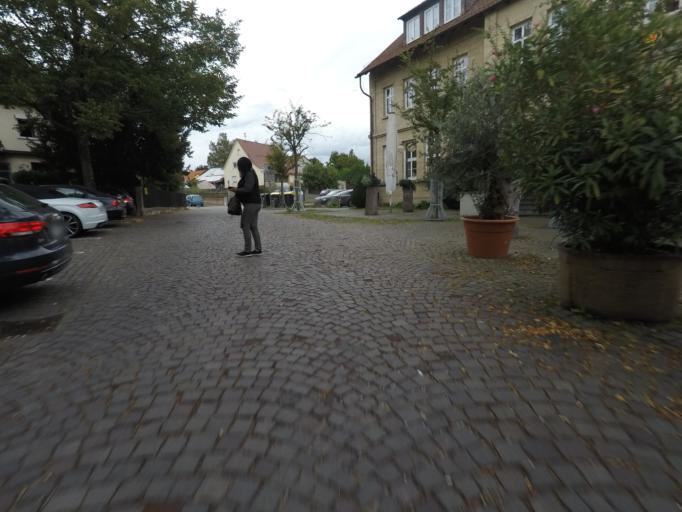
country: DE
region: Baden-Wuerttemberg
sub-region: Regierungsbezirk Stuttgart
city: Leinfelden-Echterdingen
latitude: 48.6891
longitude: 9.1696
